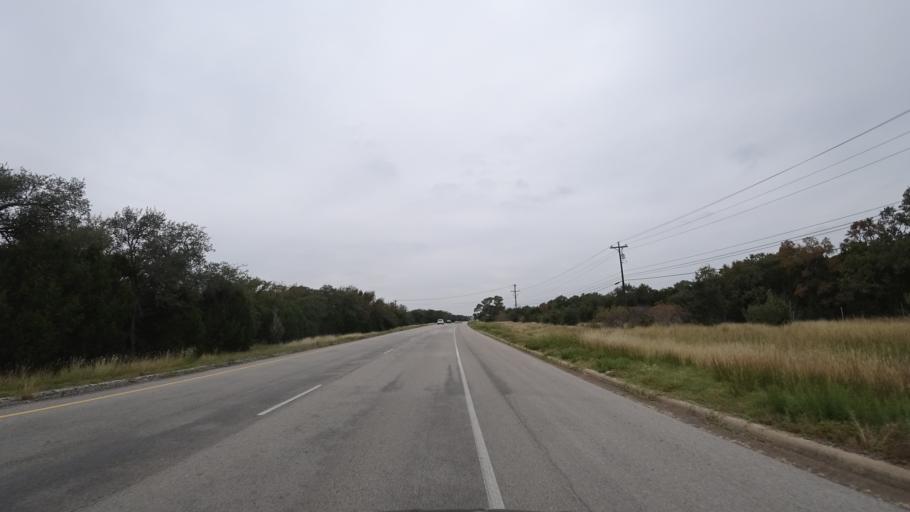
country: US
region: Texas
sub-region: Travis County
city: Shady Hollow
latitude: 30.1887
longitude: -97.9156
